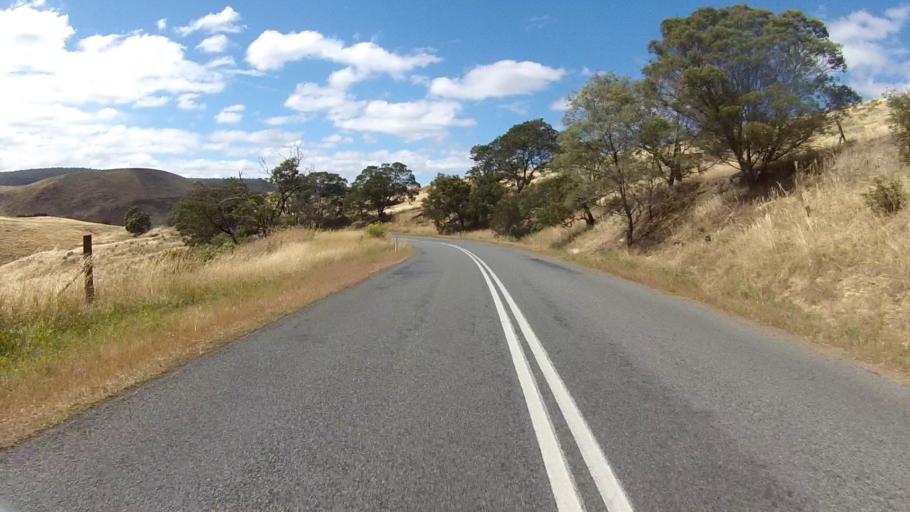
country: AU
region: Tasmania
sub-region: Brighton
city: Bridgewater
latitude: -42.5709
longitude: 147.3948
